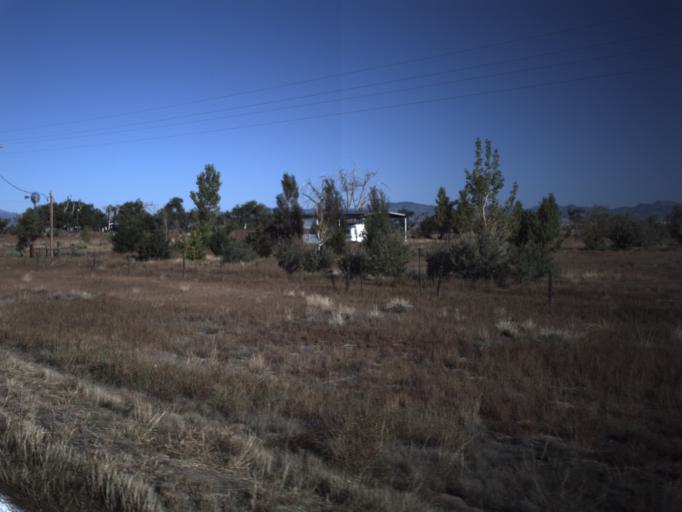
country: US
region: Utah
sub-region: Washington County
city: Enterprise
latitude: 37.7238
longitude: -113.6962
